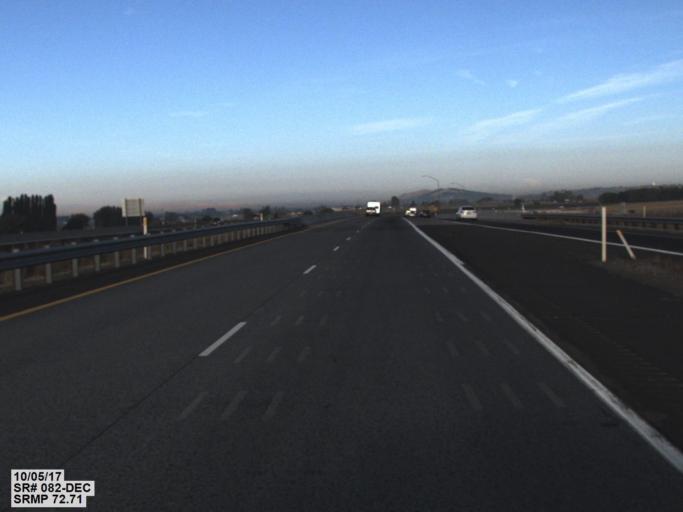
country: US
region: Washington
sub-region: Yakima County
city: Grandview
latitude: 46.2704
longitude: -119.9220
